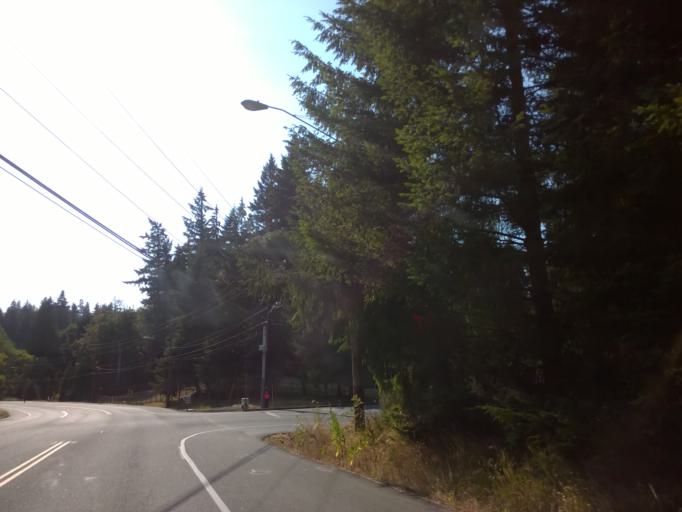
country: US
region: Washington
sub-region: King County
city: Redmond
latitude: 47.6894
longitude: -122.0884
